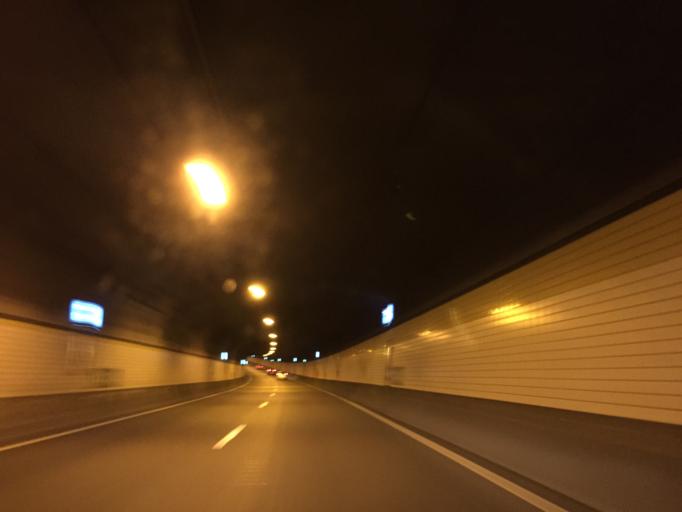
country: NL
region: South Holland
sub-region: Gemeente Schiedam
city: Schiedam
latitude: 51.9025
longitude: 4.3699
